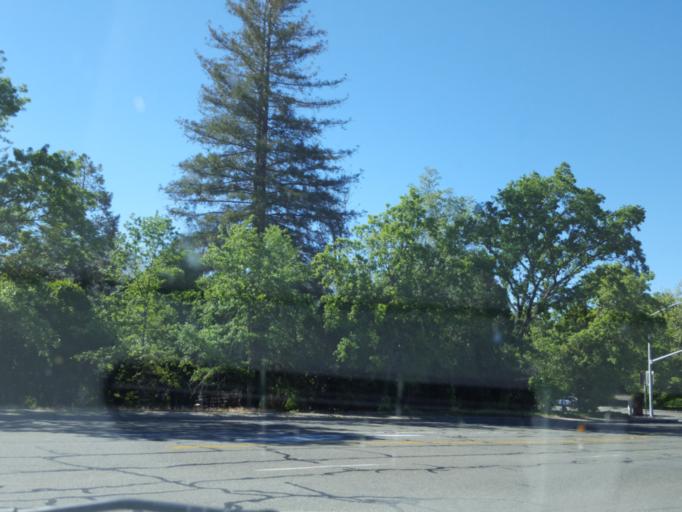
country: US
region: California
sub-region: Placer County
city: Auburn
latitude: 38.8903
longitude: -121.0764
